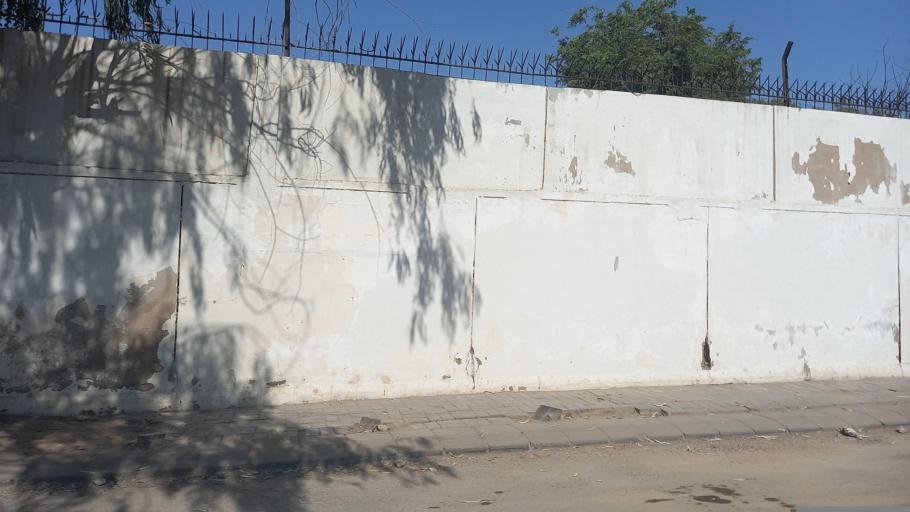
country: PK
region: Sindh
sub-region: Karachi District
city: Karachi
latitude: 24.8010
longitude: 67.0462
